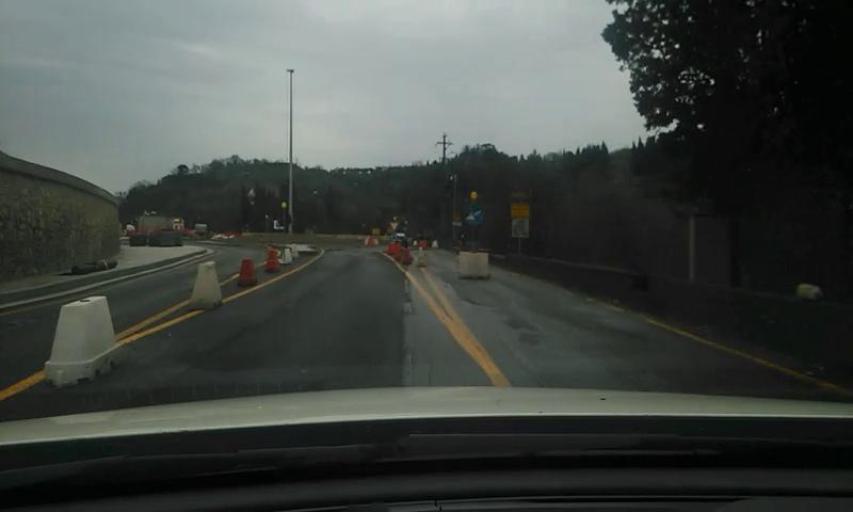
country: IT
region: Tuscany
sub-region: Provincia di Prato
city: Vaiano
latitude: 43.9254
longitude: 11.1271
